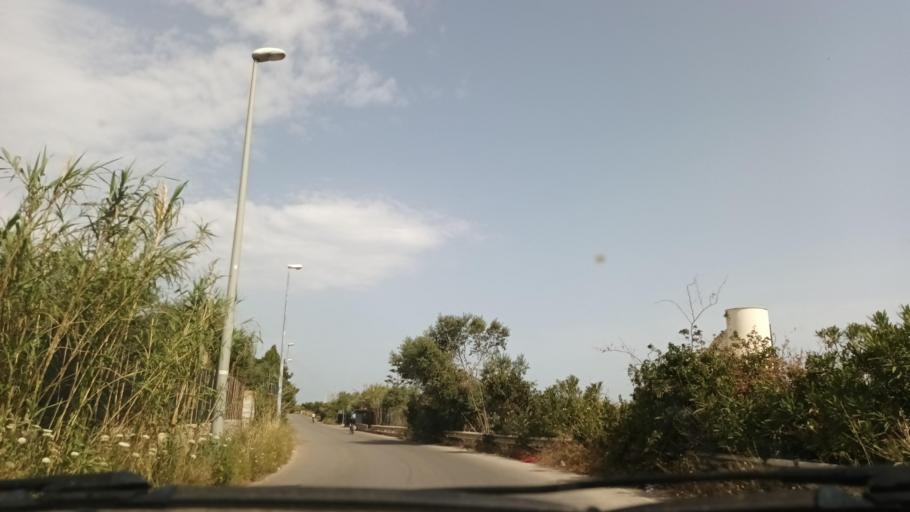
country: IT
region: Sicily
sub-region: Palermo
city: Santa Flavia
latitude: 38.1078
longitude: 13.5330
